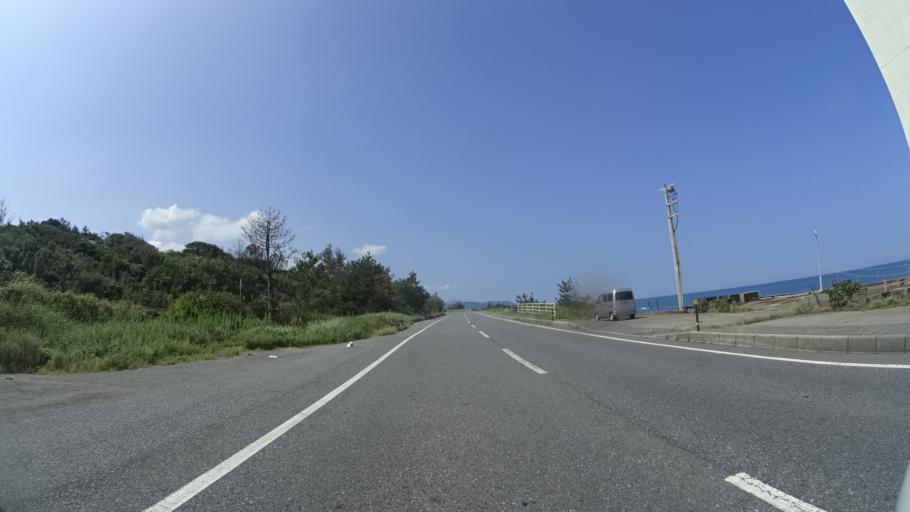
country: JP
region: Shimane
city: Masuda
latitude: 34.6831
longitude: 131.7787
